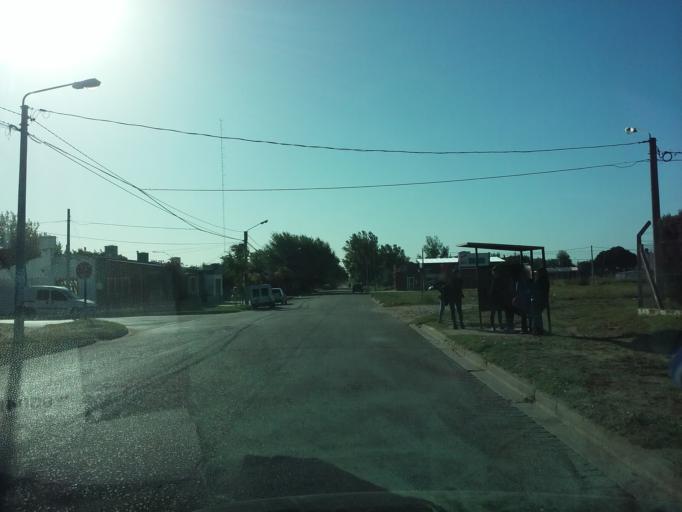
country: AR
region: La Pampa
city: Santa Rosa
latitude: -36.6423
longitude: -64.2968
